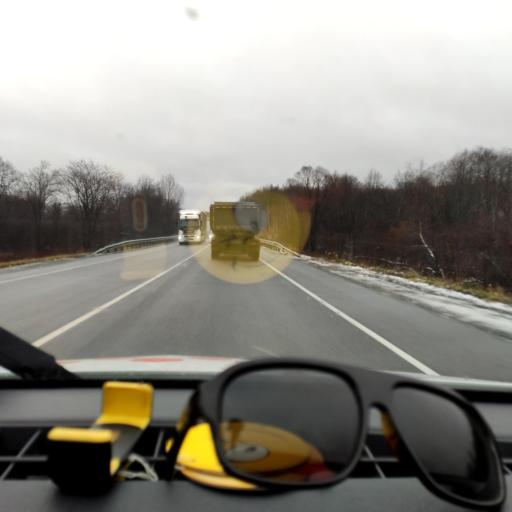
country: RU
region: Bashkortostan
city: Urman
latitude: 54.8175
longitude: 56.8628
